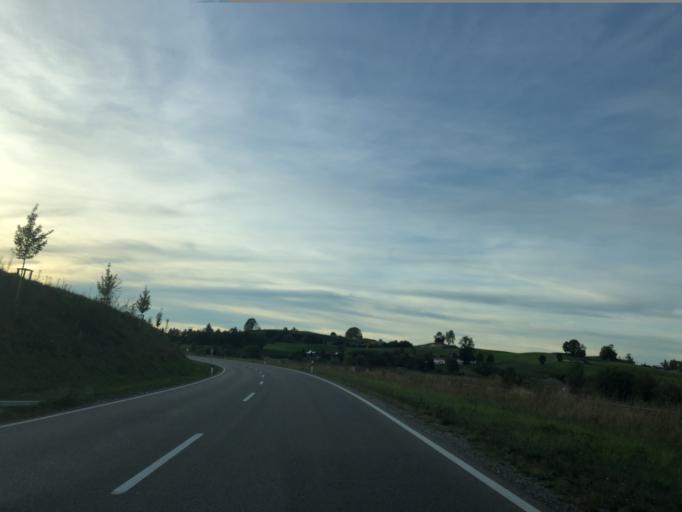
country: DE
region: Bavaria
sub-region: Swabia
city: Pfronten
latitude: 47.6082
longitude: 10.5358
